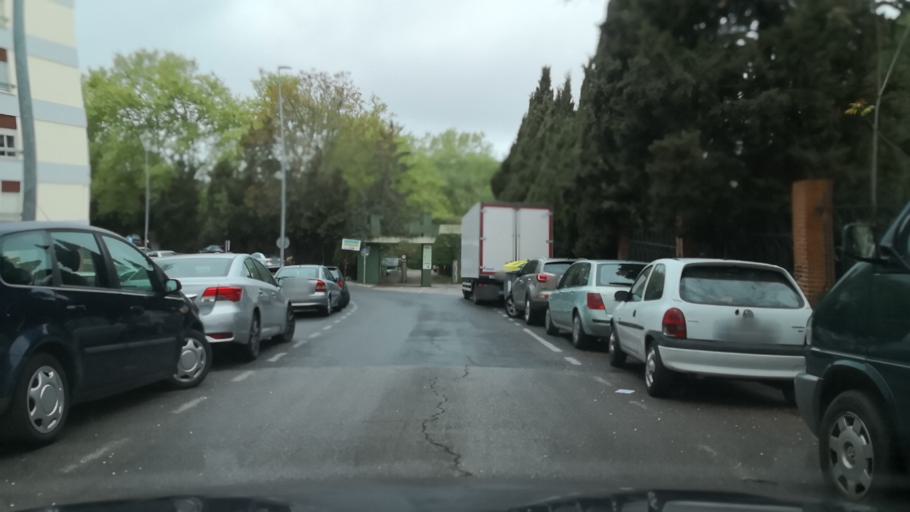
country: ES
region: Extremadura
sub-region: Provincia de Caceres
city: Caceres
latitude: 39.4749
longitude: -6.3798
